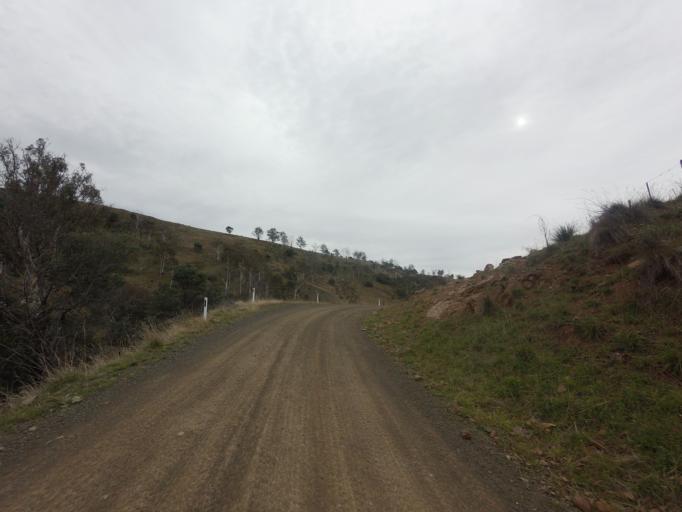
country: AU
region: Tasmania
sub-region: Derwent Valley
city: New Norfolk
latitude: -42.3621
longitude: 146.8415
